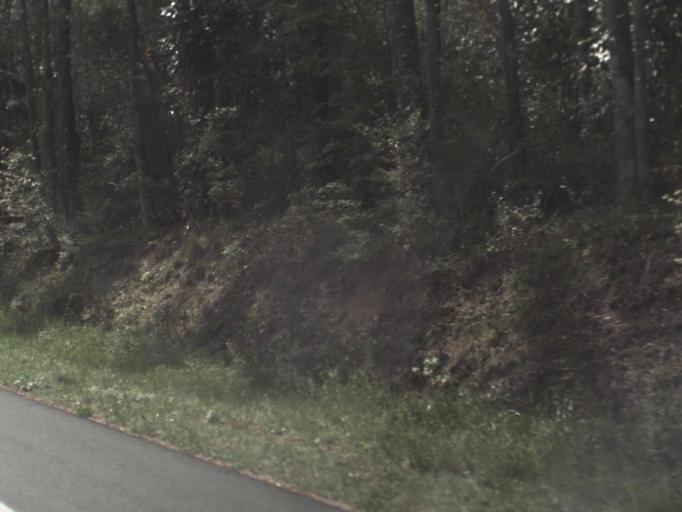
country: US
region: Alabama
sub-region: Covington County
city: Florala
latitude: 30.9656
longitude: -86.4166
